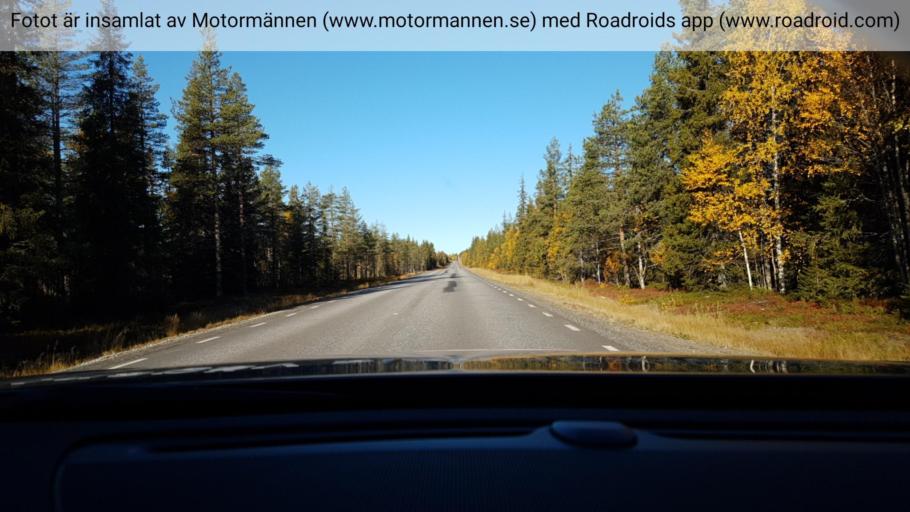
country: SE
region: Vaesterbotten
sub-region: Skelleftea Kommun
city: Storvik
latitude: 65.3567
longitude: 20.4630
